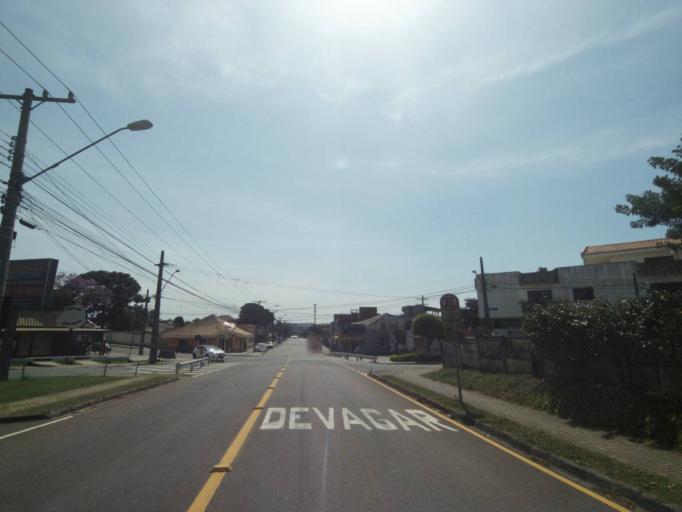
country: BR
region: Parana
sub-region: Curitiba
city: Curitiba
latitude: -25.4703
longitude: -49.3023
